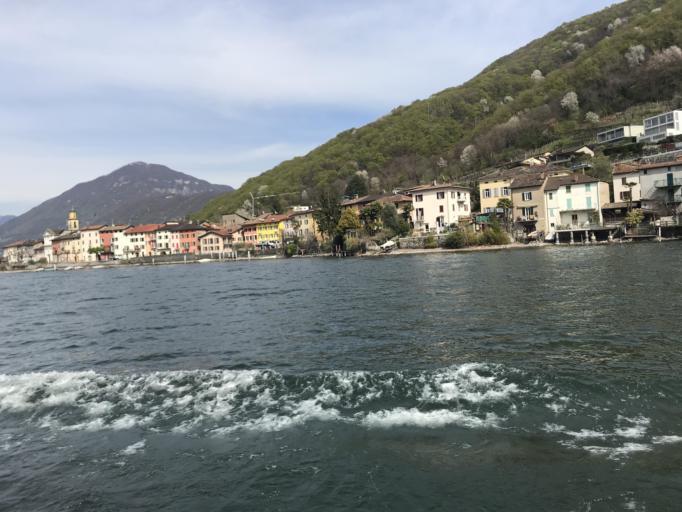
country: CH
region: Ticino
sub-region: Lugano District
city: Melide
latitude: 45.9269
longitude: 8.9354
